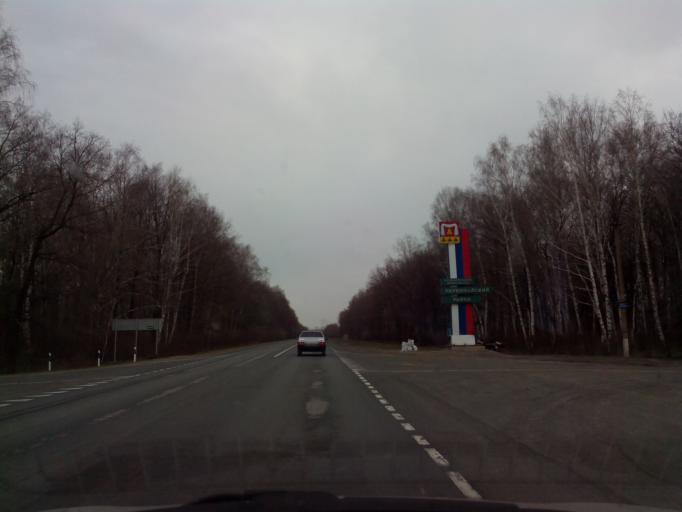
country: RU
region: Tambov
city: Michurinsk
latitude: 53.0718
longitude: 40.4290
